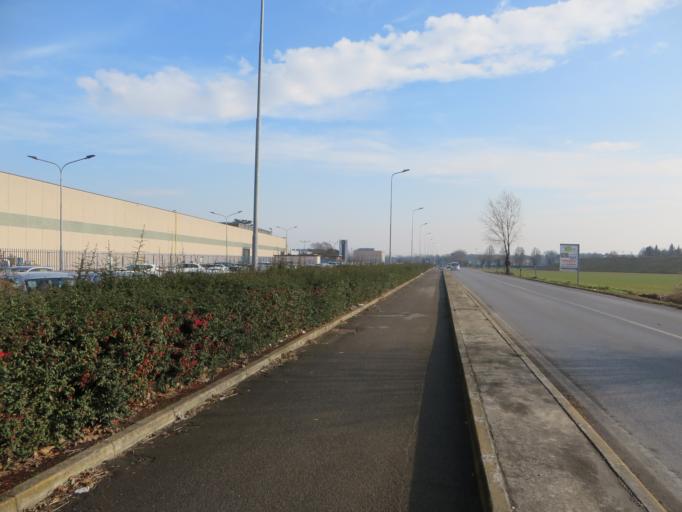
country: IT
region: Lombardy
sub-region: Provincia di Brescia
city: Torbole Casaglia
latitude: 45.5160
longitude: 10.1112
